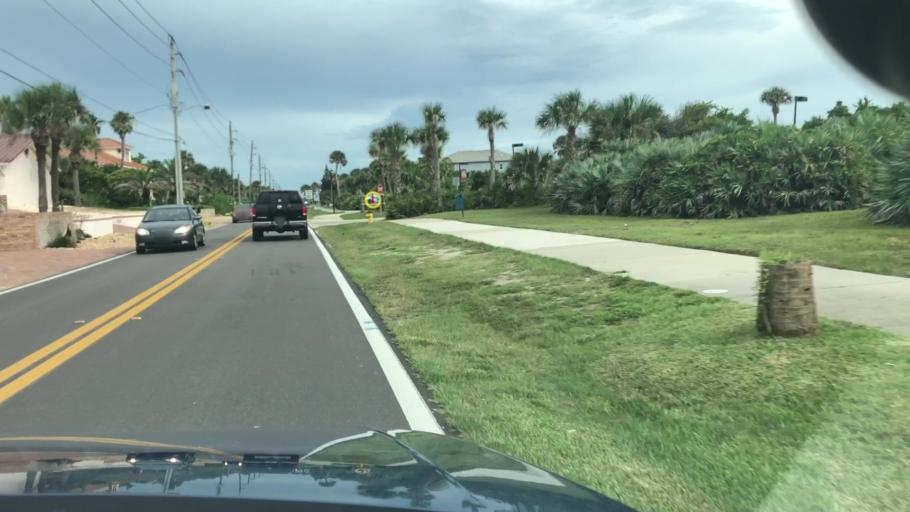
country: US
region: Florida
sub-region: Volusia County
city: Ponce Inlet
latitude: 29.1219
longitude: -80.9523
